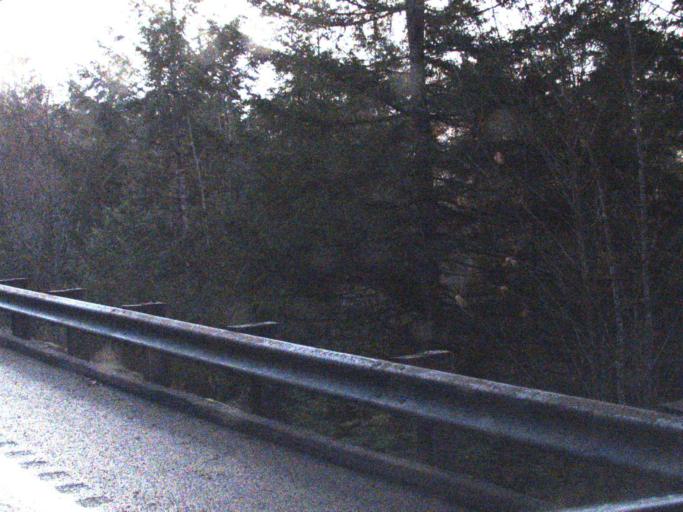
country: US
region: Washington
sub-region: Snohomish County
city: Darrington
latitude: 48.5019
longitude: -121.6488
